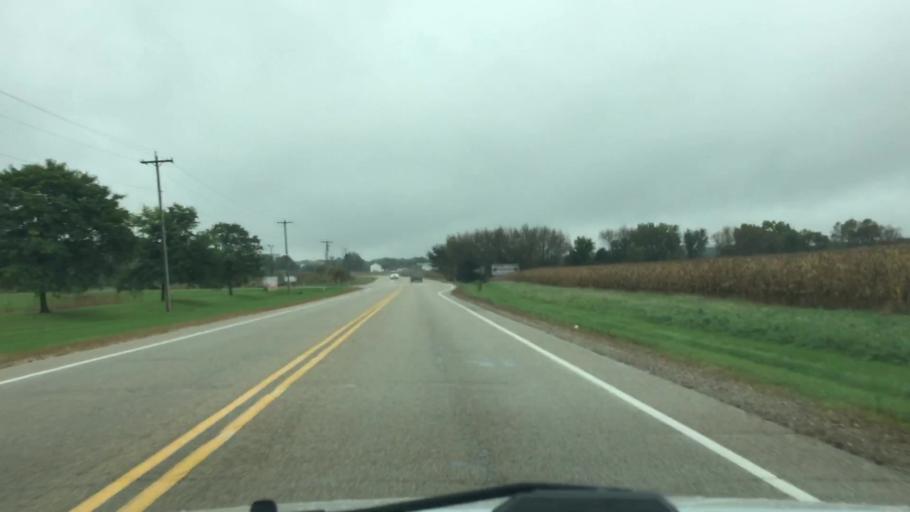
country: US
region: Wisconsin
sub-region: Walworth County
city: Whitewater
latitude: 42.8498
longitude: -88.7188
